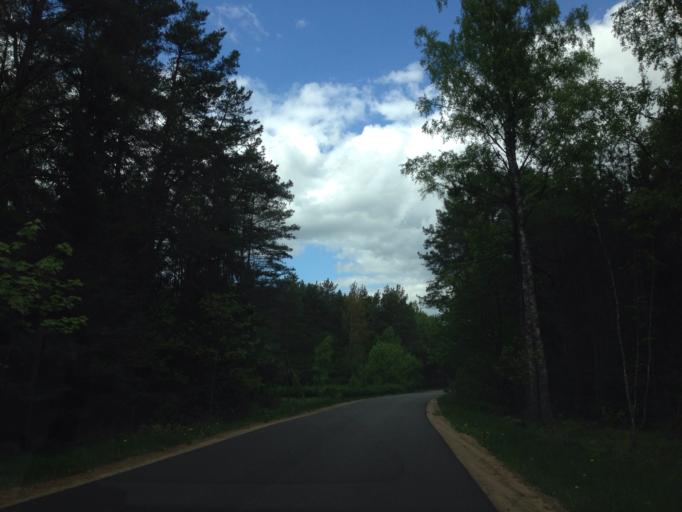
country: PL
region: Podlasie
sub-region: Powiat grajewski
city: Radzilow
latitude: 53.3469
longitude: 22.5973
